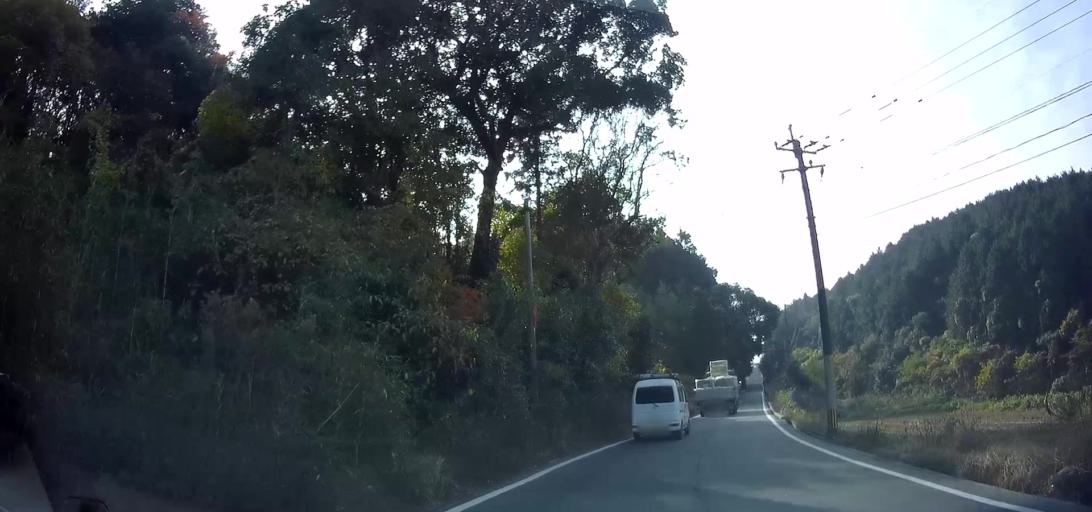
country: JP
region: Nagasaki
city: Shimabara
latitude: 32.6931
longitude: 130.2063
